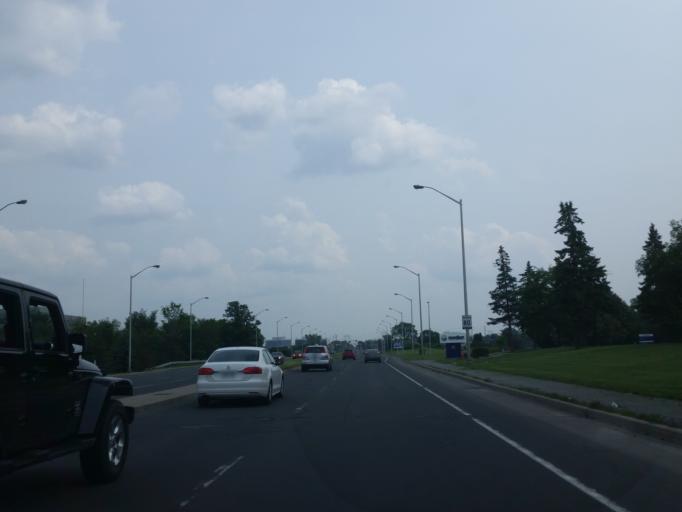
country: CA
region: Ontario
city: Bells Corners
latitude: 45.3419
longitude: -75.9159
